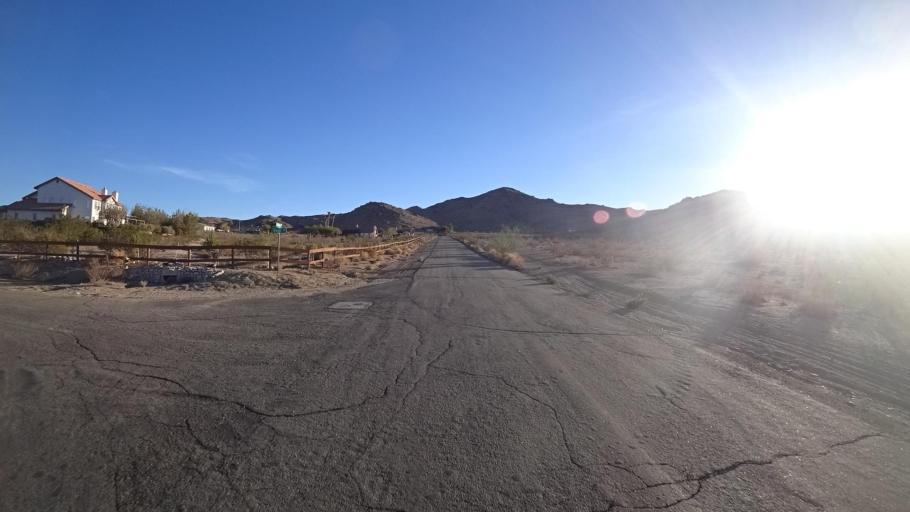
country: US
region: California
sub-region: Kern County
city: Ridgecrest
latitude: 35.5759
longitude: -117.6523
